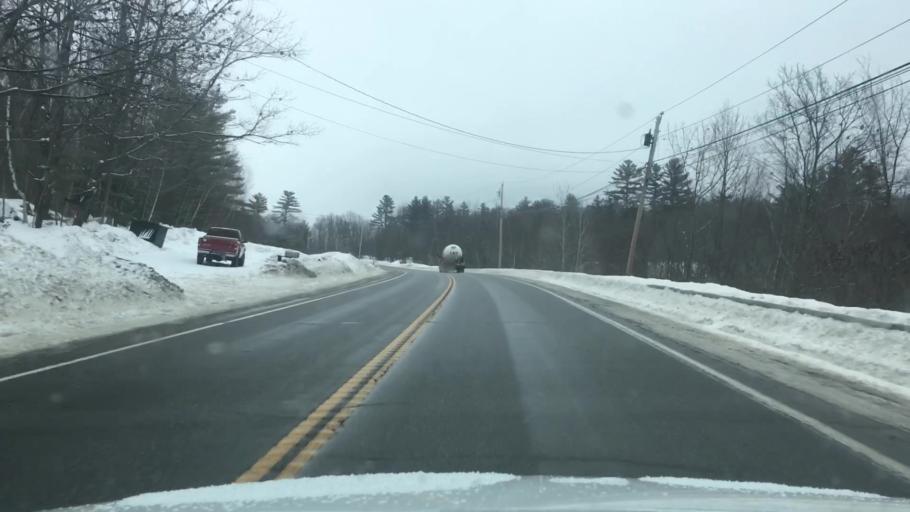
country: US
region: Maine
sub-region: Franklin County
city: Wilton
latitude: 44.5758
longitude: -70.3254
